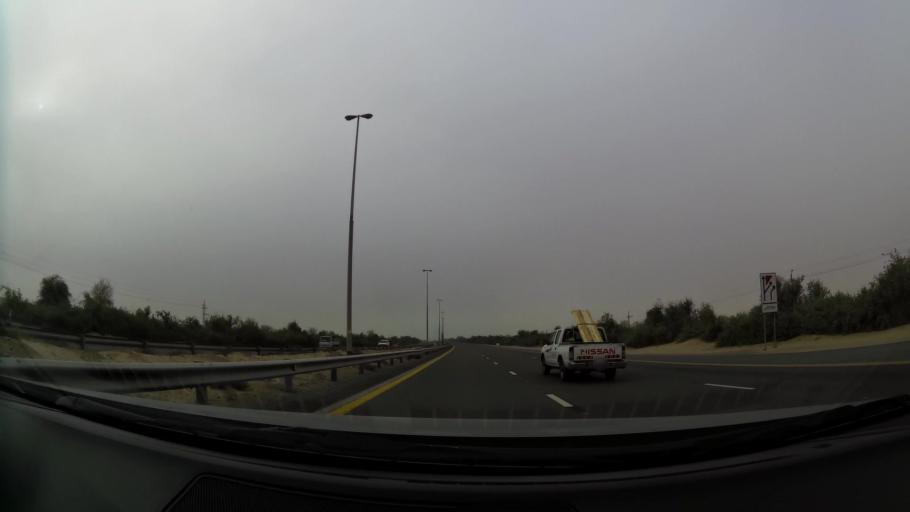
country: AE
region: Dubai
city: Dubai
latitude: 25.0599
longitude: 55.4159
